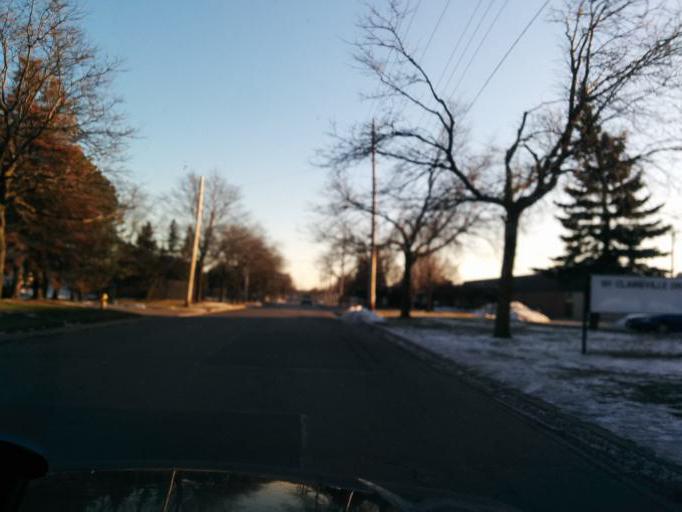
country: CA
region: Ontario
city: Etobicoke
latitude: 43.7419
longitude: -79.6259
